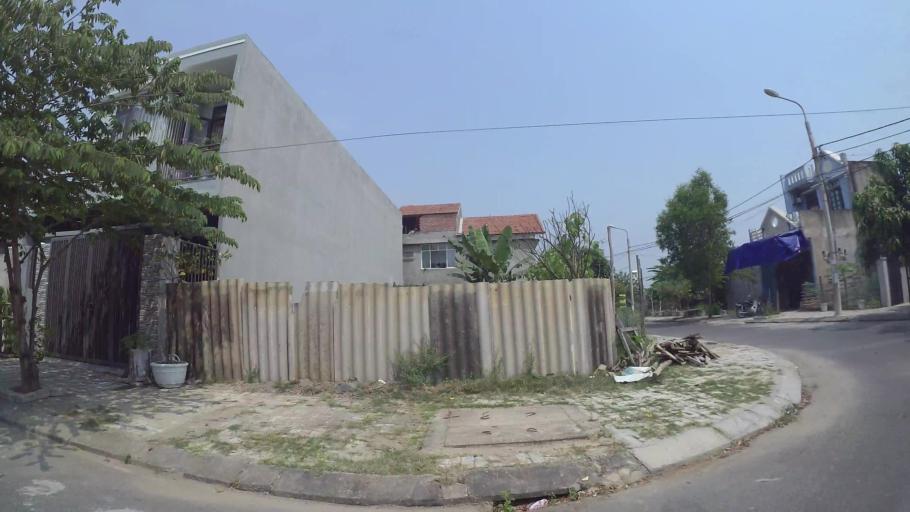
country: VN
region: Da Nang
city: Cam Le
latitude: 15.9863
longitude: 108.2161
